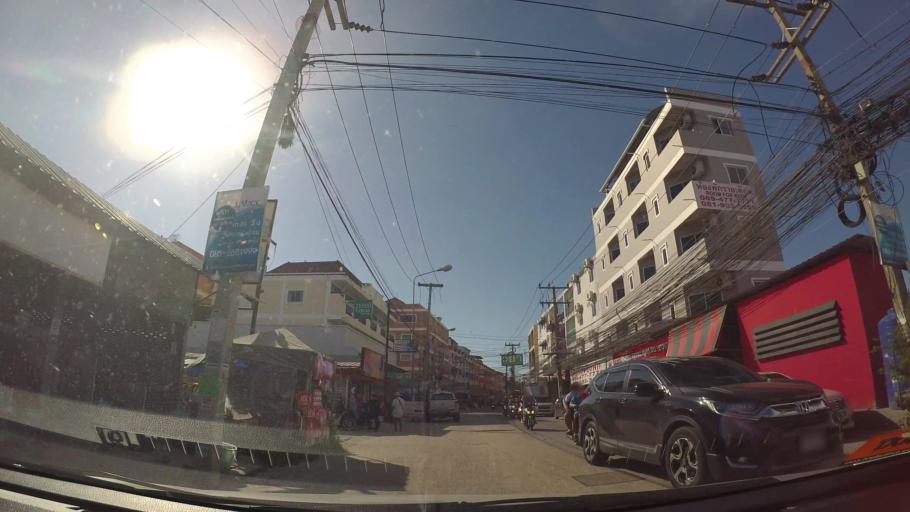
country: TH
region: Chon Buri
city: Phatthaya
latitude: 12.9148
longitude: 100.8799
